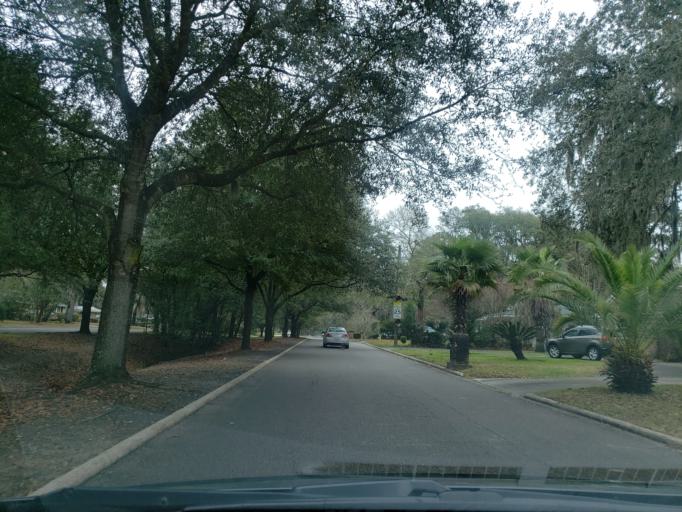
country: US
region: Georgia
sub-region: Chatham County
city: Montgomery
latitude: 31.9725
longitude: -81.1458
